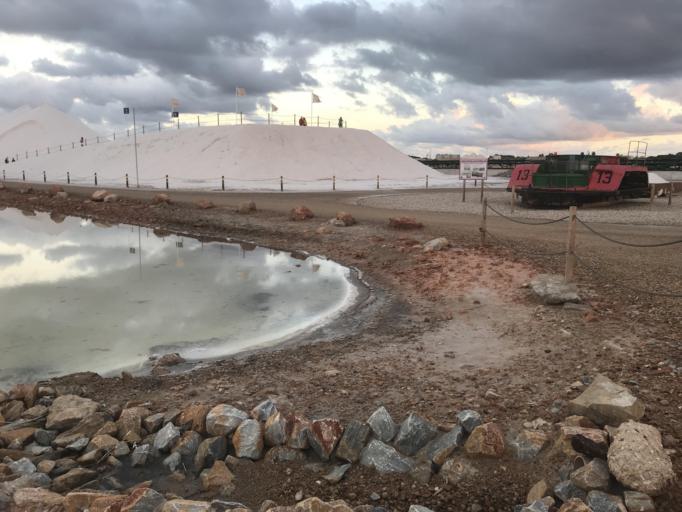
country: ES
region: Valencia
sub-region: Provincia de Alicante
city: Torrevieja
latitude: 37.9805
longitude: -0.7071
